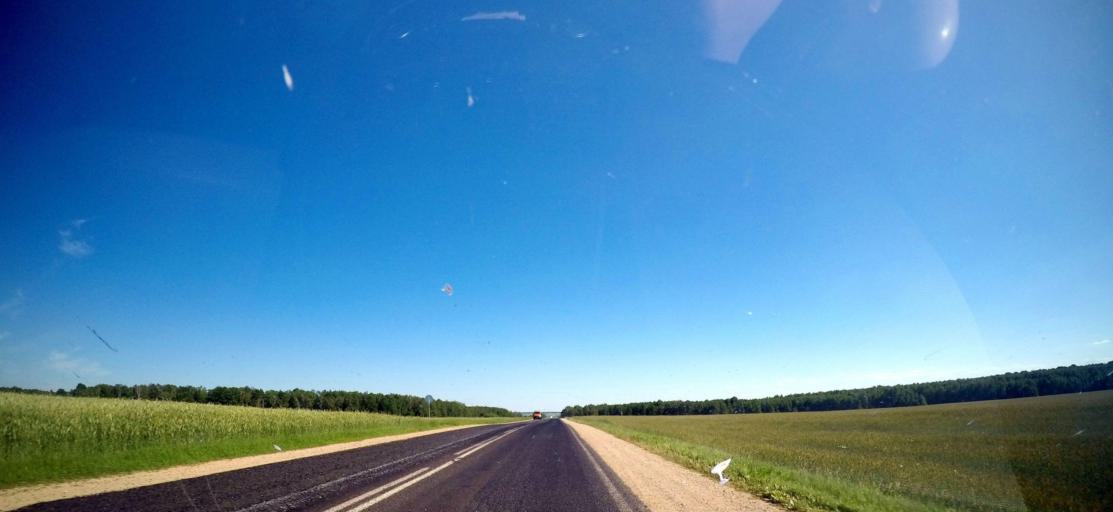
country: BY
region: Grodnenskaya
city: Vyalikaya Byerastavitsa
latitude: 53.2239
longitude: 23.9938
